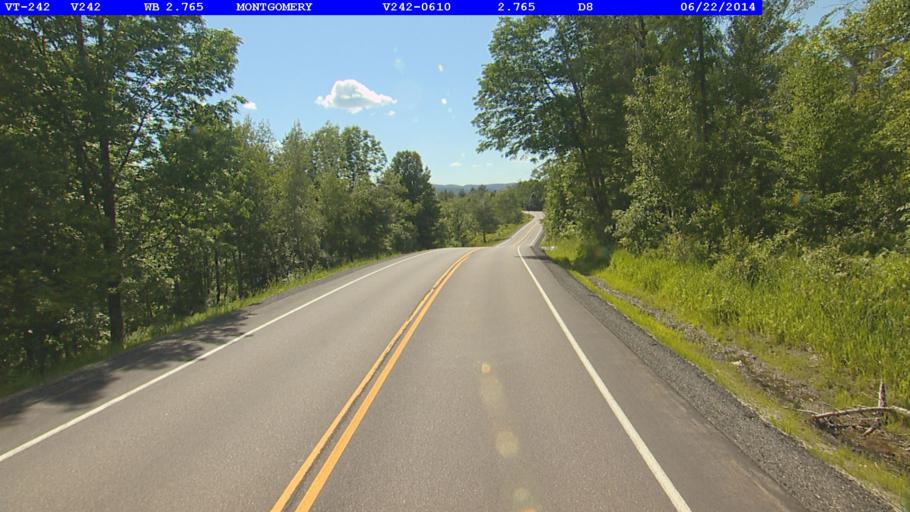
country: US
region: Vermont
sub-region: Franklin County
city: Richford
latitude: 44.8810
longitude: -72.5573
